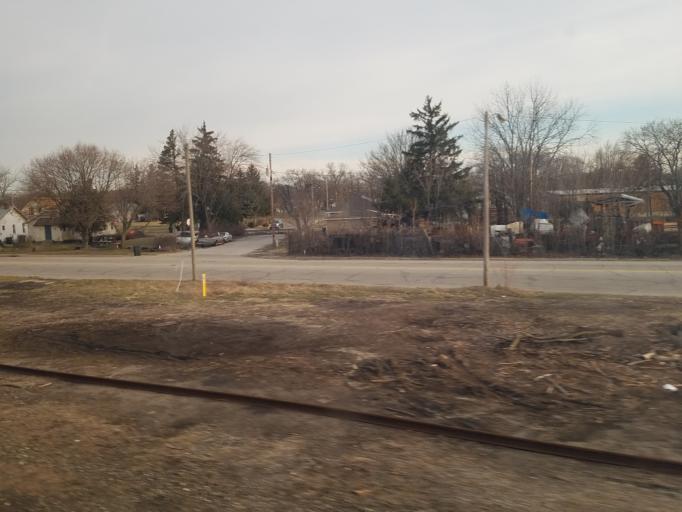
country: US
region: Indiana
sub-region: Saint Joseph County
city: South Bend
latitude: 41.6770
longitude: -86.2848
